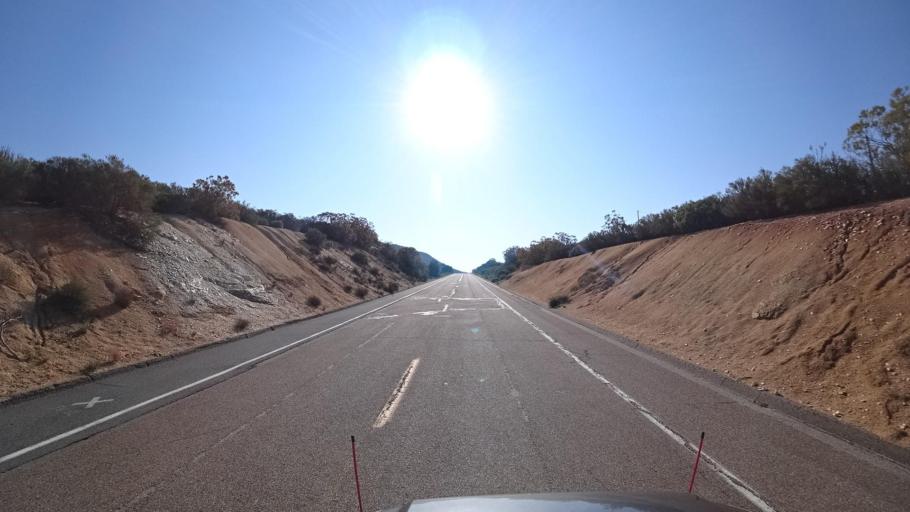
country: US
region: California
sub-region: San Diego County
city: Pine Valley
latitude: 32.8154
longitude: -116.5147
